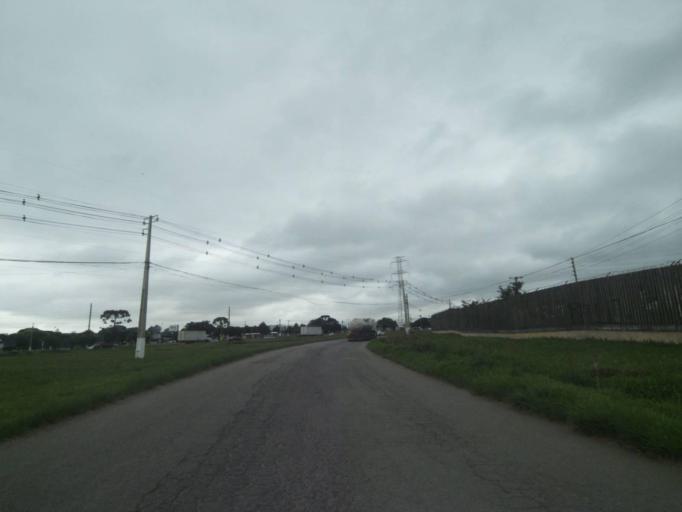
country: BR
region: Parana
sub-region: Araucaria
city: Araucaria
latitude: -25.5249
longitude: -49.3322
